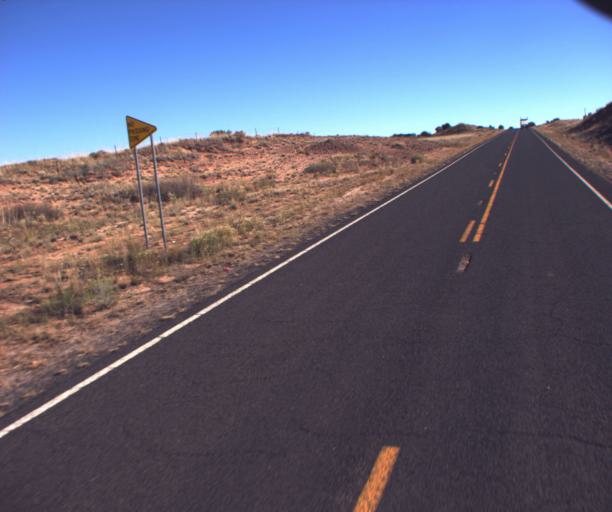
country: US
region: Arizona
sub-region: Apache County
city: Houck
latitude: 35.3889
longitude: -109.4981
